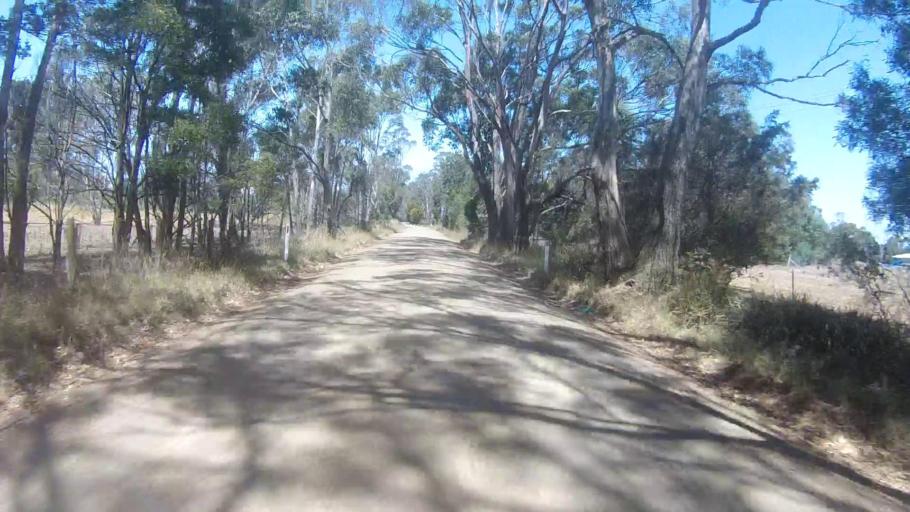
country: AU
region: Tasmania
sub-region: Sorell
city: Sorell
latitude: -42.8558
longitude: 147.8335
